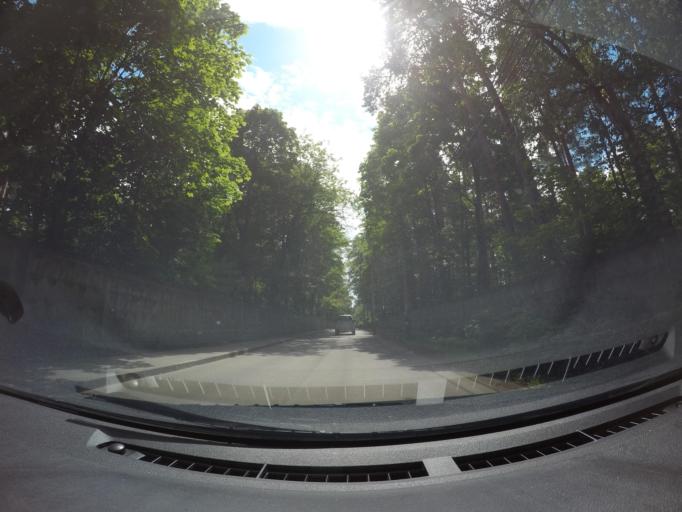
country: RU
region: Moskovskaya
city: Malakhovka
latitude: 55.6443
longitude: 38.0401
